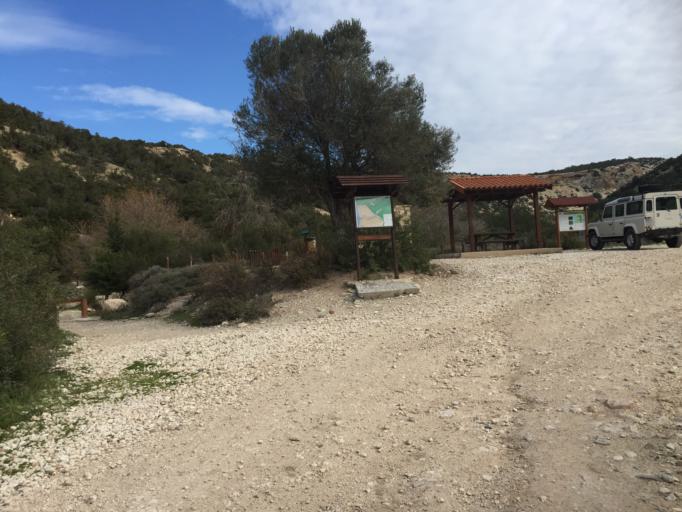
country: CY
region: Pafos
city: Pegeia
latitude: 34.9204
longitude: 32.3377
